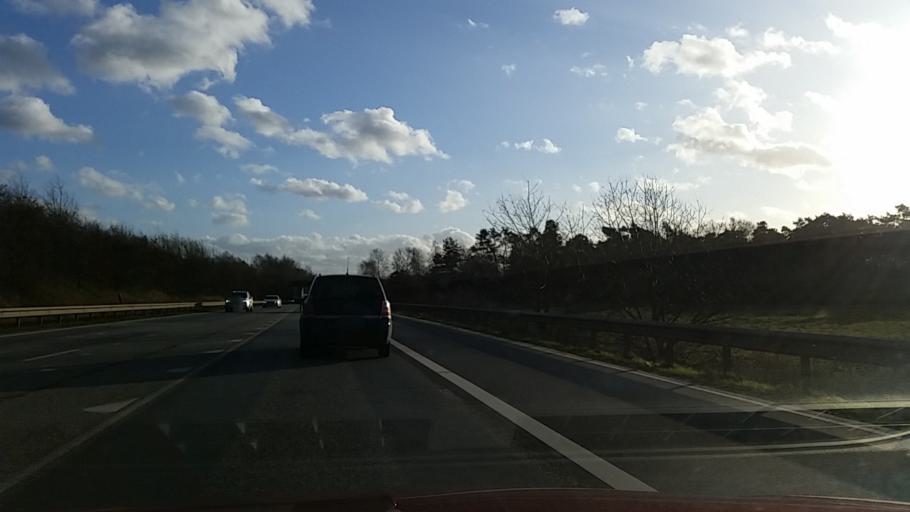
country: DE
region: Schleswig-Holstein
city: Glinde
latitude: 53.5569
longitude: 10.2313
